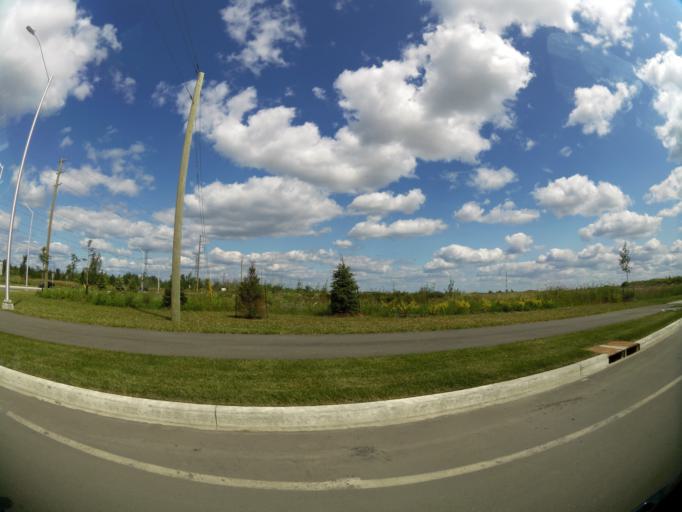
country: CA
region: Ontario
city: Ottawa
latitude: 45.4408
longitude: -75.5090
